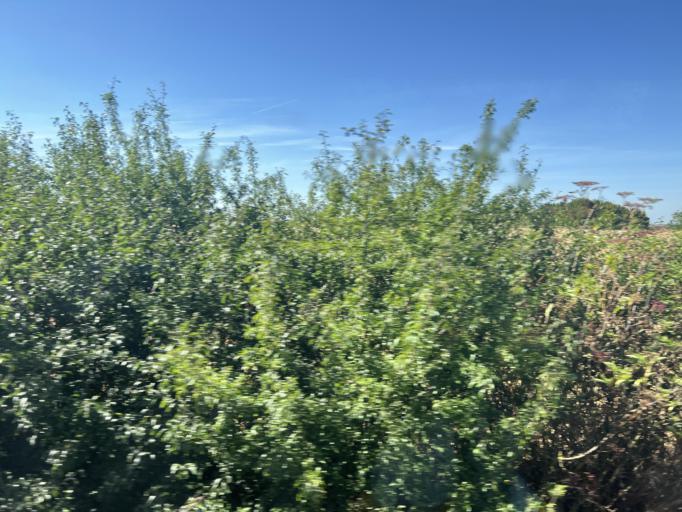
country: GB
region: England
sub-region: Lincolnshire
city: Heckington
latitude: 52.9835
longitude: -0.3257
